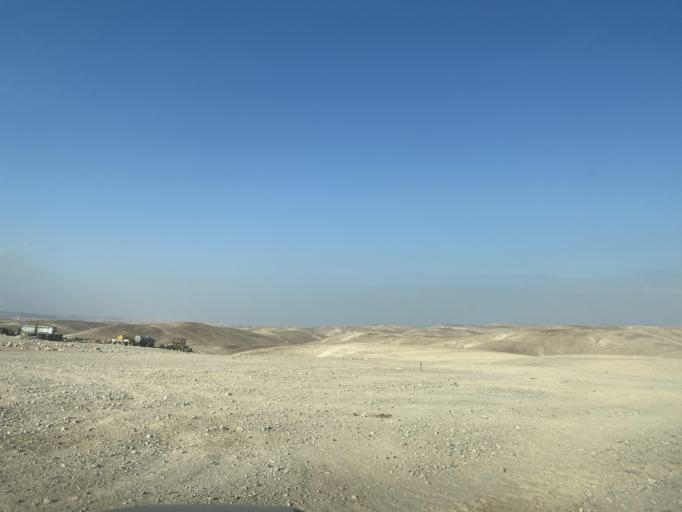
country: PS
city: `Arab ar Rashaydah
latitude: 31.5222
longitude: 35.3052
